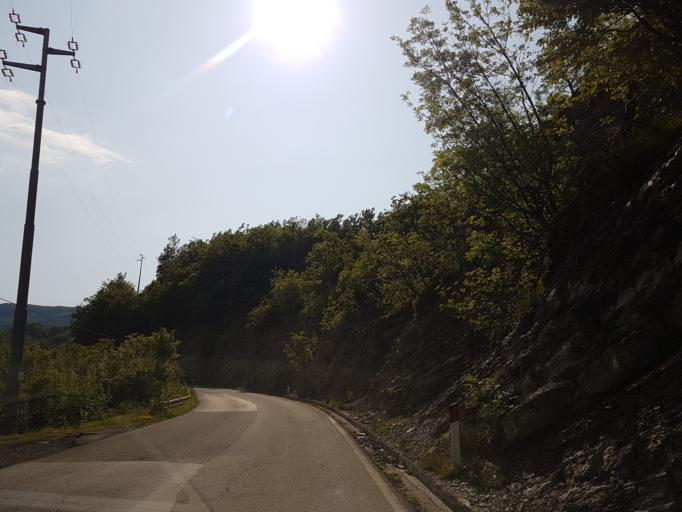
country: IT
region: Emilia-Romagna
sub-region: Forli-Cesena
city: San Piero in Bagno
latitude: 43.8156
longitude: 11.9437
